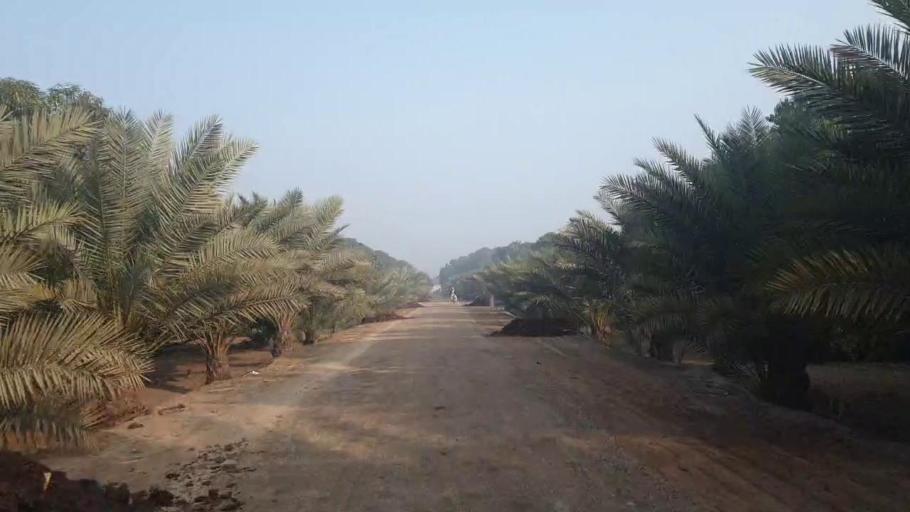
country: PK
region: Sindh
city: Tando Adam
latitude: 25.7916
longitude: 68.6403
